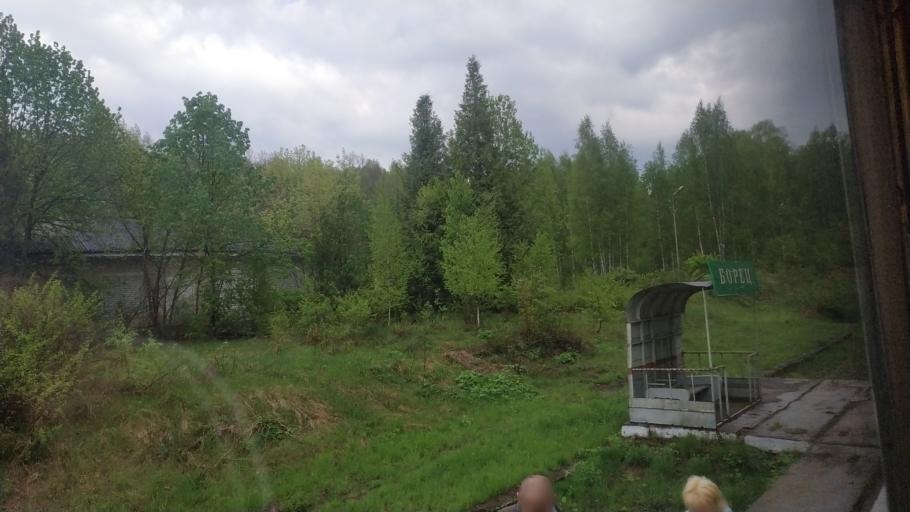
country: RU
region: Kaluga
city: Baryatino
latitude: 54.3109
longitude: 34.3403
